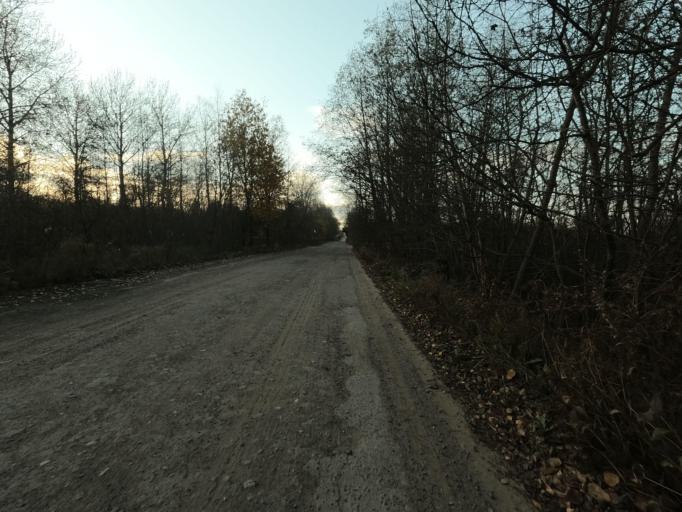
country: RU
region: Leningrad
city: Mga
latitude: 59.7635
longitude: 31.2515
